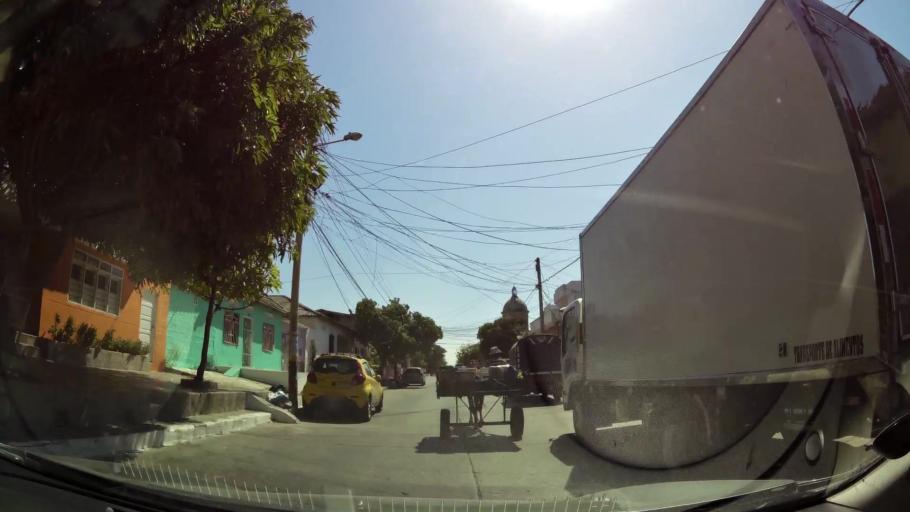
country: CO
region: Atlantico
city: Barranquilla
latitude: 10.9735
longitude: -74.7879
